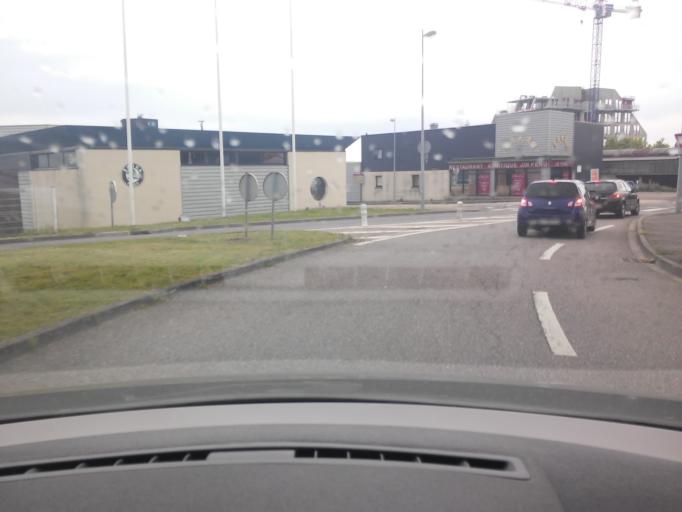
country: FR
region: Lorraine
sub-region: Departement de Meurthe-et-Moselle
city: Laxou
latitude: 48.6910
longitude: 6.1337
